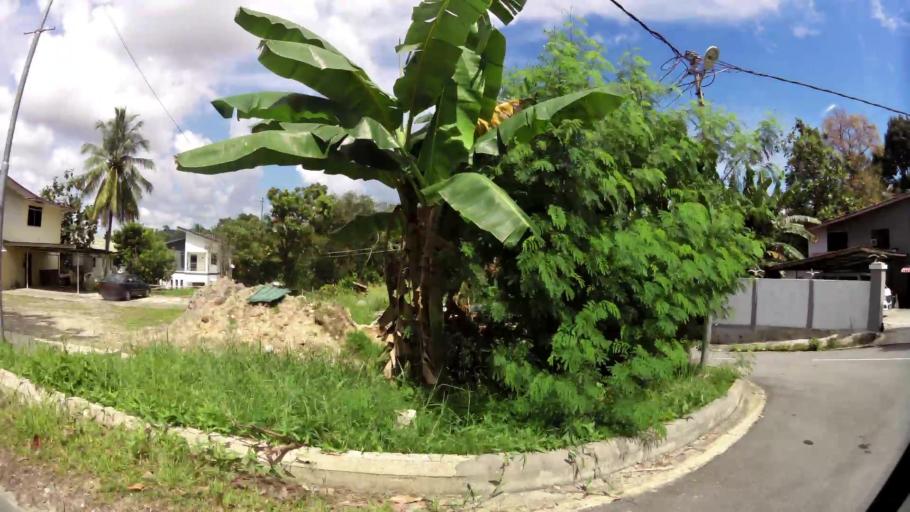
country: BN
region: Brunei and Muara
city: Bandar Seri Begawan
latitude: 4.9742
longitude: 114.9491
